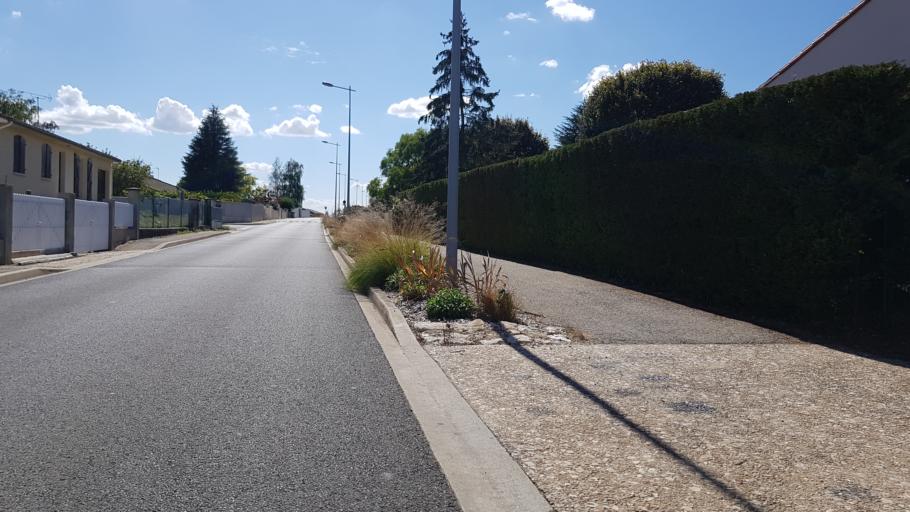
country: FR
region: Poitou-Charentes
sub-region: Departement des Deux-Sevres
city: Vouille
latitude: 46.3137
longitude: -0.3604
